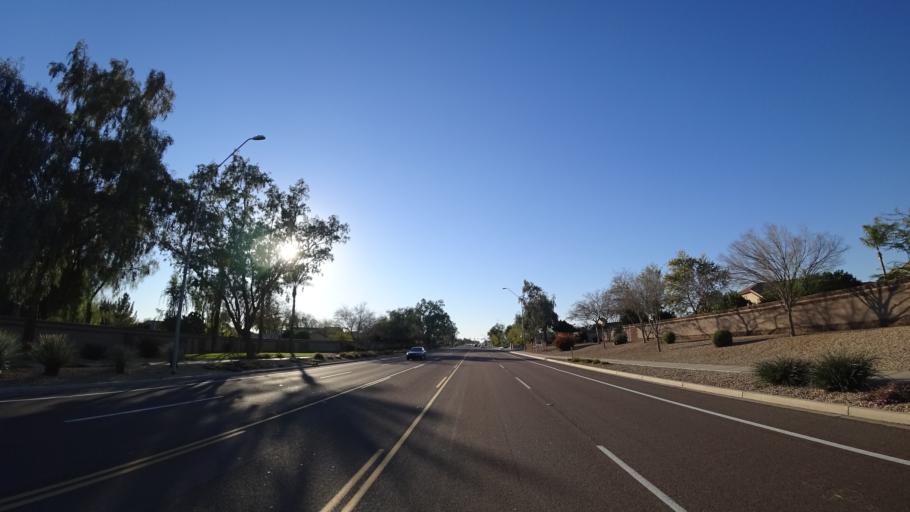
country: US
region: Arizona
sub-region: Maricopa County
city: Sun City
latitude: 33.6816
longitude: -112.2342
